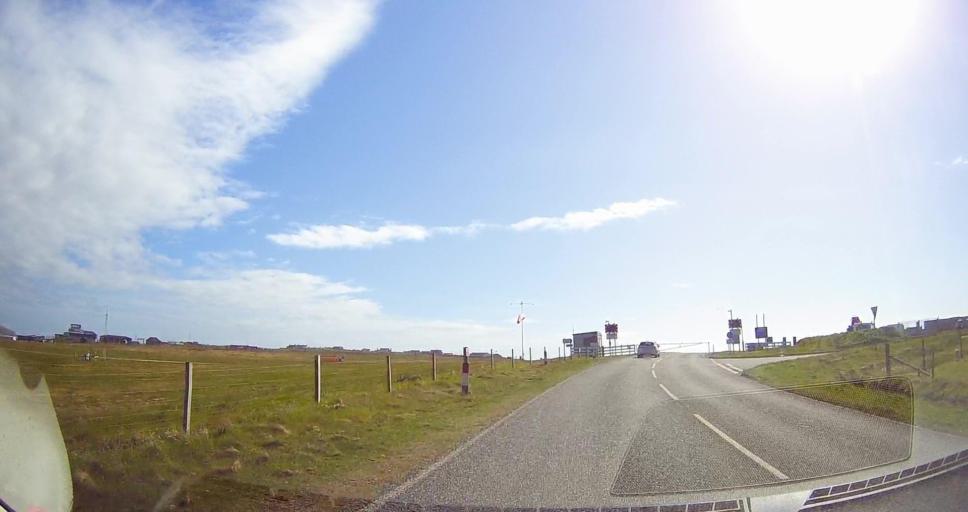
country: GB
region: Scotland
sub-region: Shetland Islands
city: Sandwick
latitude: 59.8829
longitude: -1.3024
